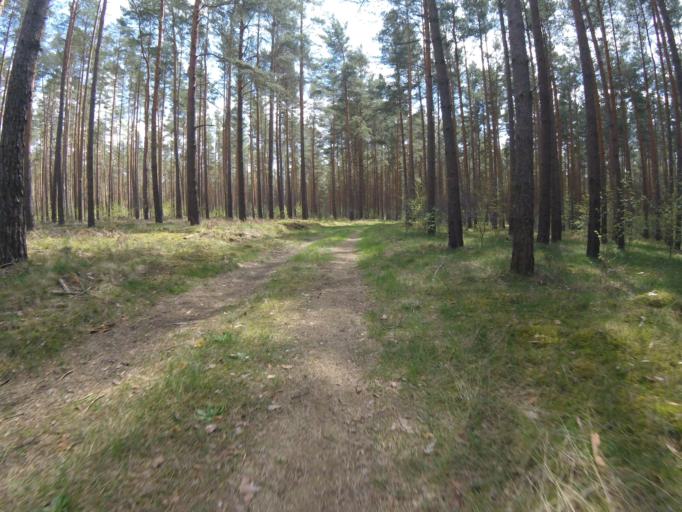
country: DE
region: Brandenburg
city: Gross Koris
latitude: 52.1866
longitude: 13.6858
